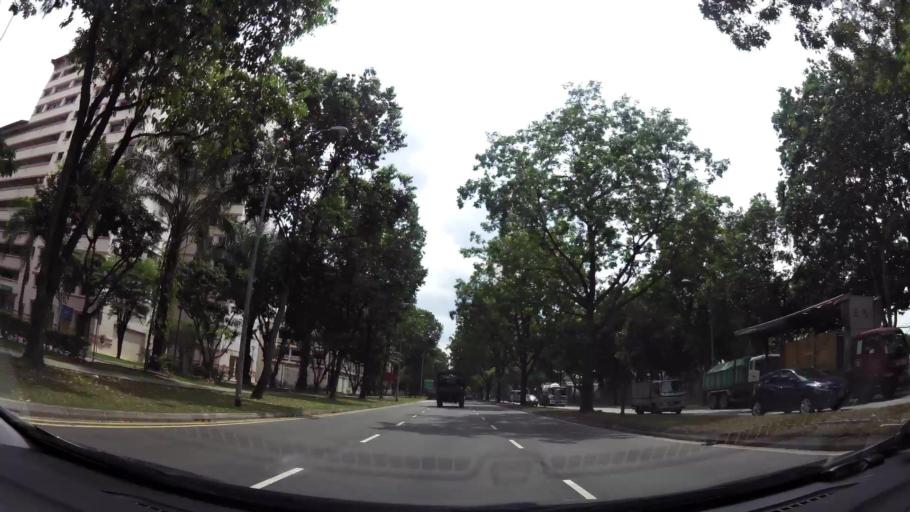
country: MY
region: Johor
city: Johor Bahru
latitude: 1.3998
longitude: 103.7432
